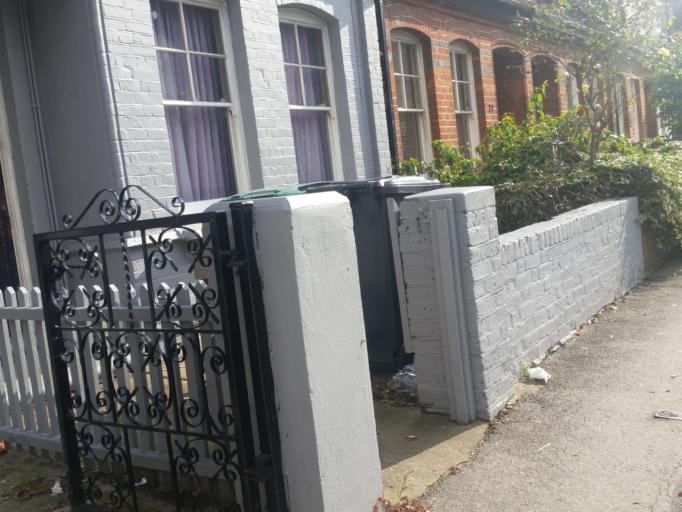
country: GB
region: England
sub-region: Greater London
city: Harringay
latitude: 51.5923
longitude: -0.1038
